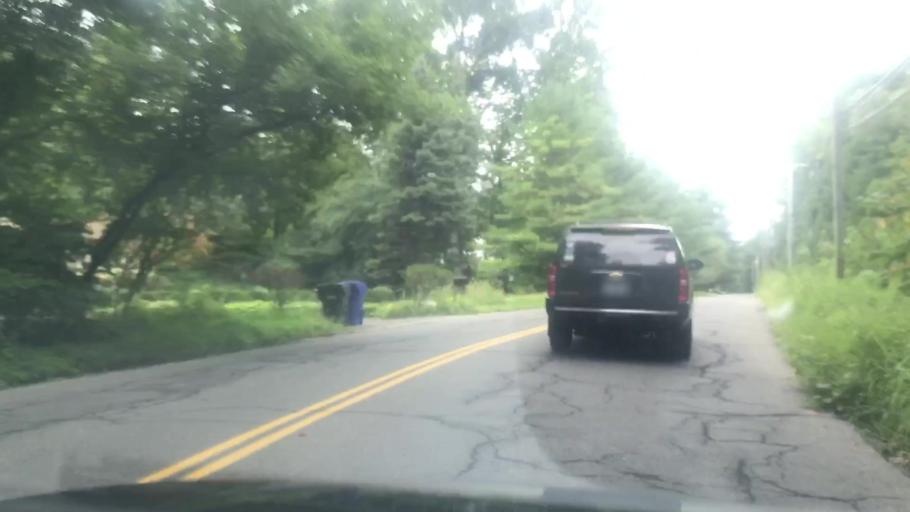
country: US
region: Connecticut
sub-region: Litchfield County
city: New Milford
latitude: 41.5971
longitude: -73.4147
